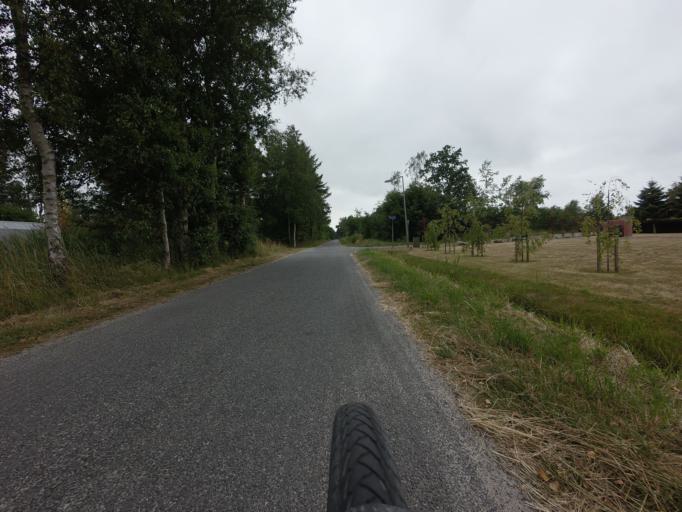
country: DK
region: North Denmark
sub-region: Laeso Kommune
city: Byrum
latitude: 57.2861
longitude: 10.9371
